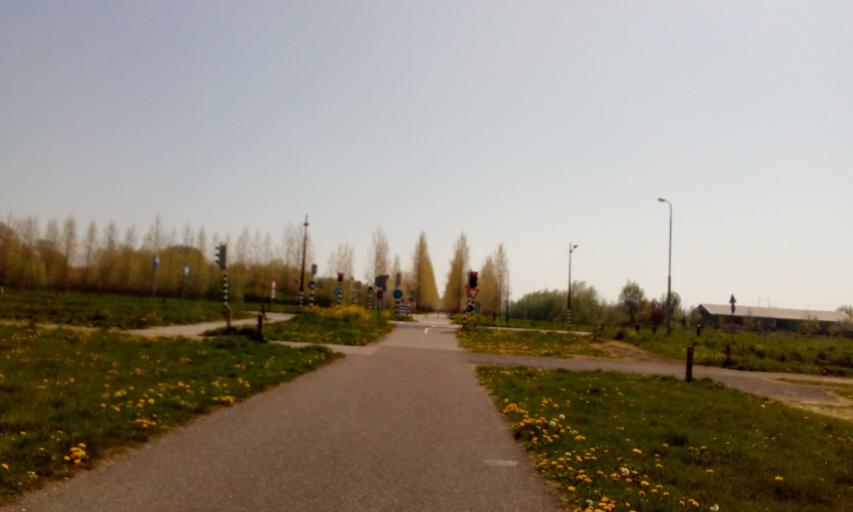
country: NL
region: South Holland
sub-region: Gemeente Hillegom
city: Hillegom
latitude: 52.2622
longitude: 4.6088
